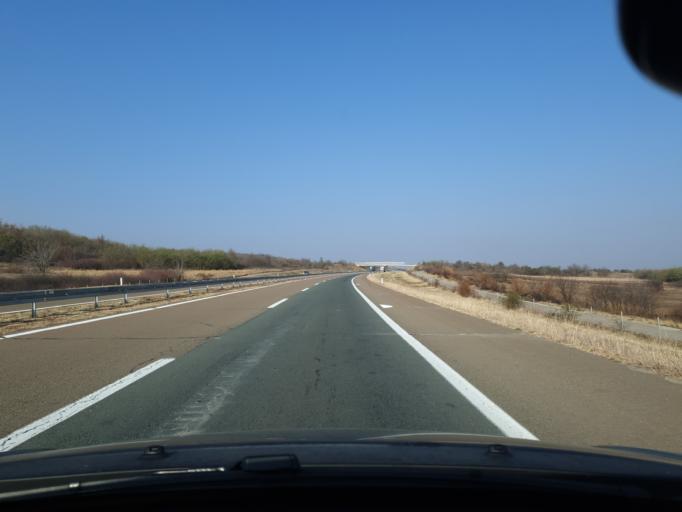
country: RS
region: Central Serbia
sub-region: Nisavski Okrug
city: Doljevac
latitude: 43.2396
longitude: 21.8185
